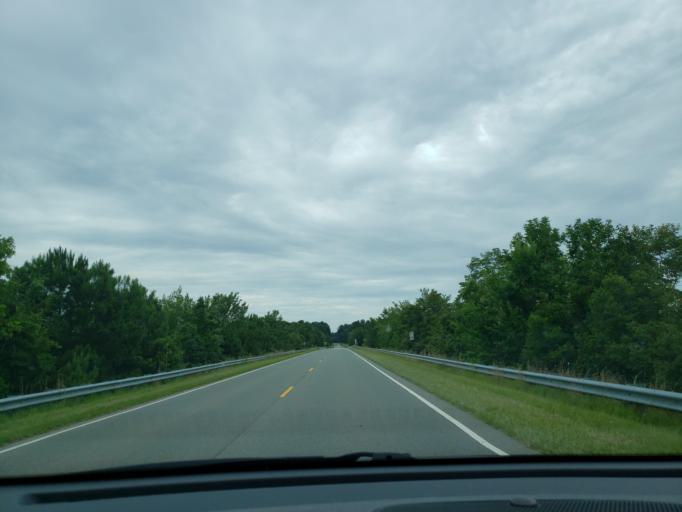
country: US
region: North Carolina
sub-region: Chatham County
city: Fearrington Village
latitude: 35.7478
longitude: -79.0066
